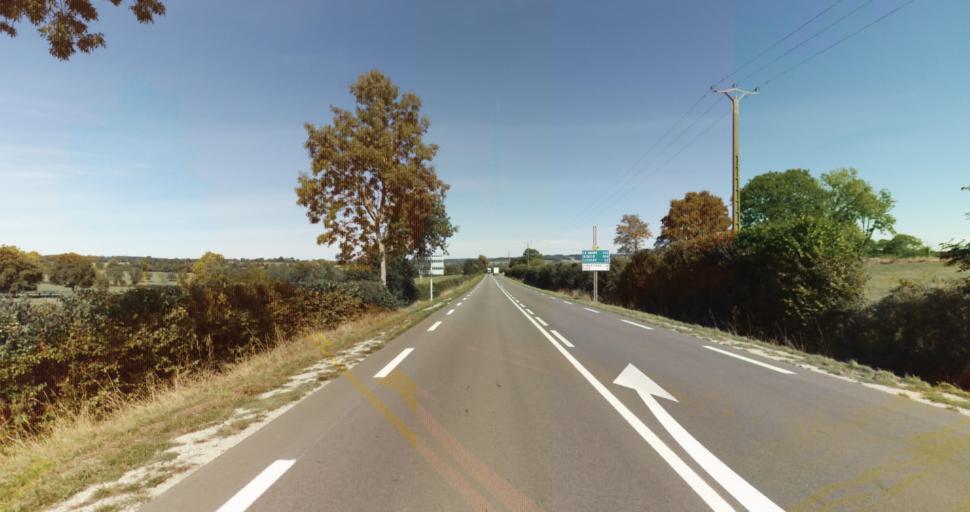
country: FR
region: Lower Normandy
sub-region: Departement de l'Orne
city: Gace
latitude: 48.7474
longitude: 0.2707
